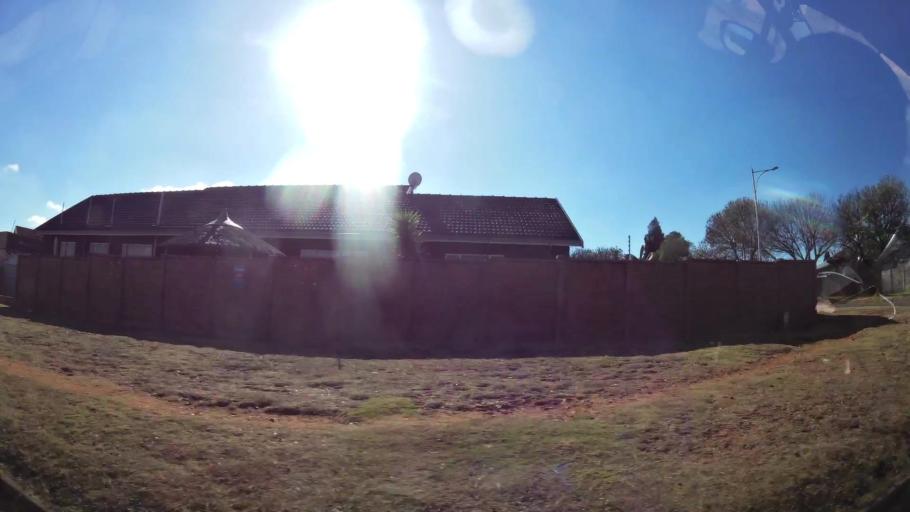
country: ZA
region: Gauteng
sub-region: City of Johannesburg Metropolitan Municipality
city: Roodepoort
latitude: -26.1398
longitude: 27.8238
